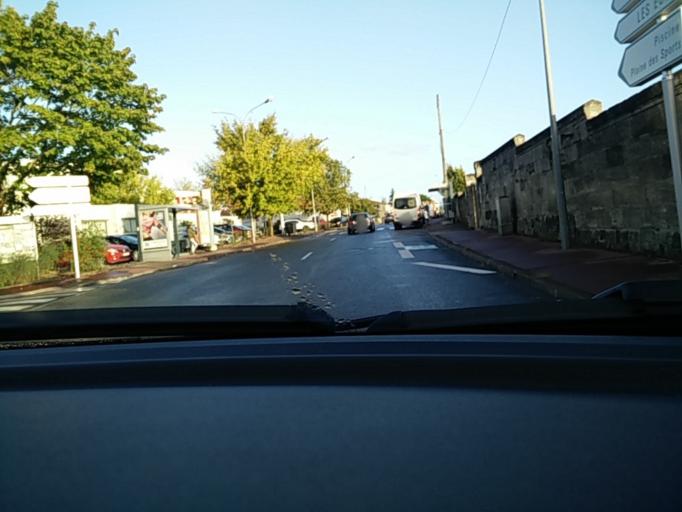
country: FR
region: Aquitaine
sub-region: Departement de la Gironde
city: Le Bouscat
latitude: 44.8666
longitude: -0.5958
